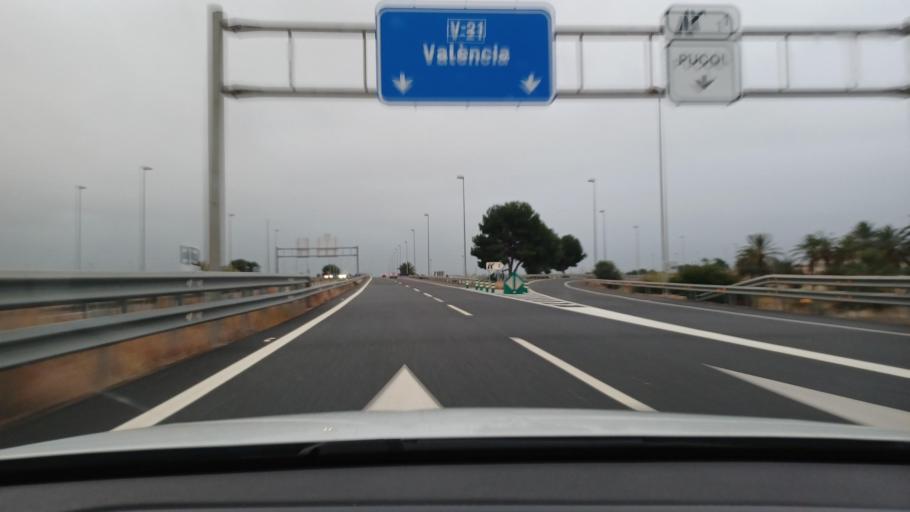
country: ES
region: Valencia
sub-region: Provincia de Valencia
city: Pucol
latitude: 39.6305
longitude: -0.3019
